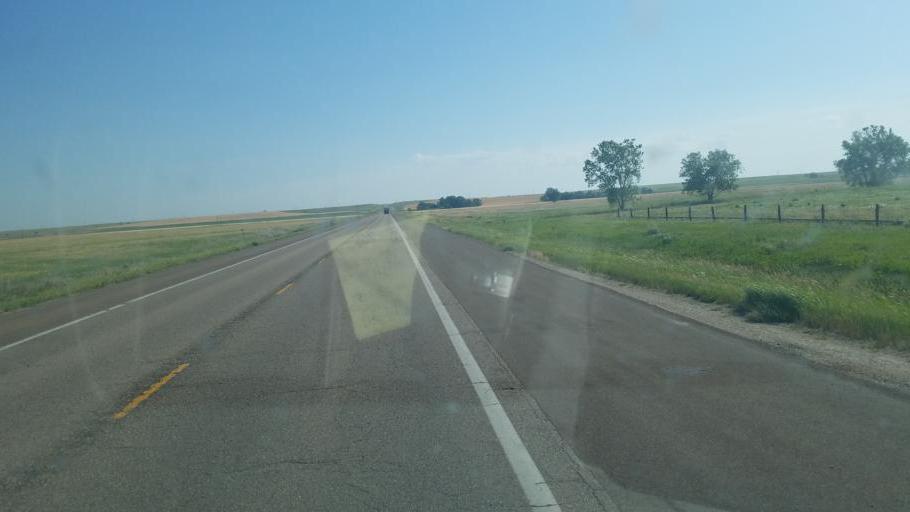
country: US
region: Kansas
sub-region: Barton County
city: Great Bend
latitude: 38.3712
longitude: -98.6911
